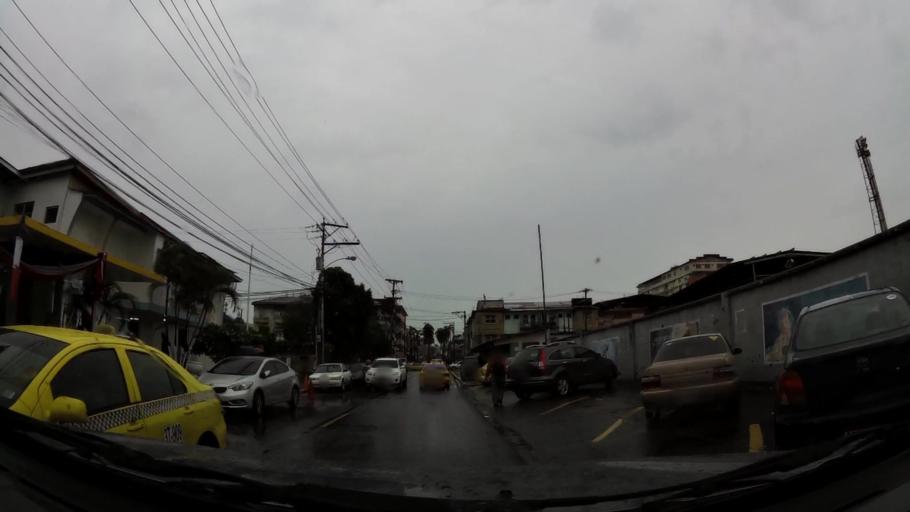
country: PA
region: Colon
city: Colon
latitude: 9.3564
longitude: -79.8969
